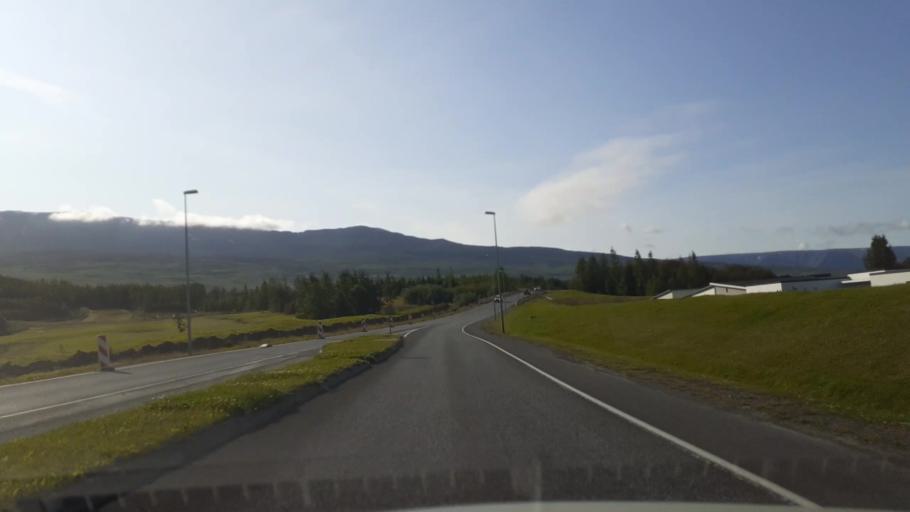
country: IS
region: Northeast
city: Akureyri
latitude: 65.6719
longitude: -18.1191
